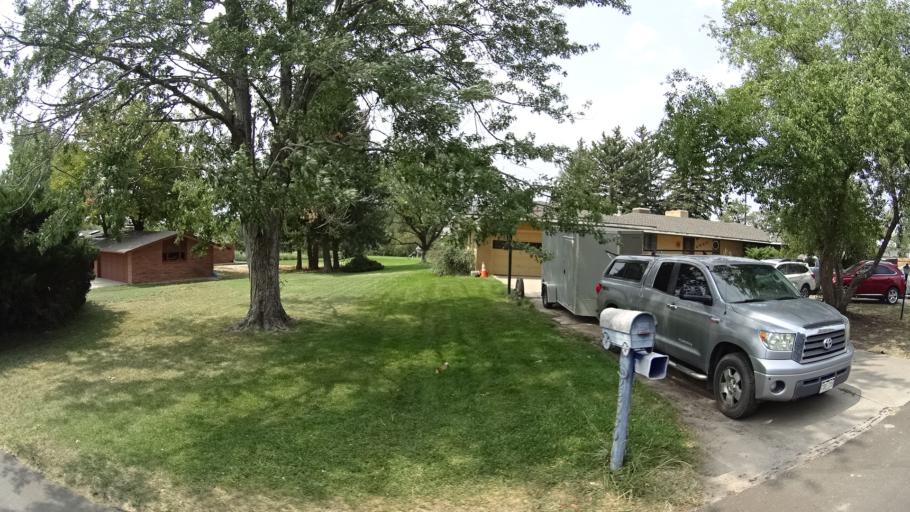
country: US
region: Colorado
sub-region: El Paso County
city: Colorado Springs
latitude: 38.8250
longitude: -104.7765
